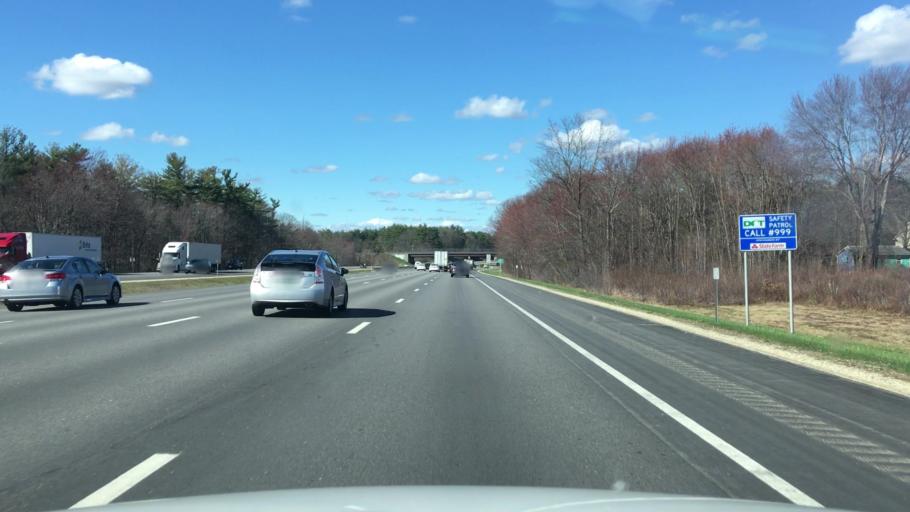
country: US
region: New Hampshire
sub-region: Rockingham County
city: Seabrook
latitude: 42.9020
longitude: -70.8780
